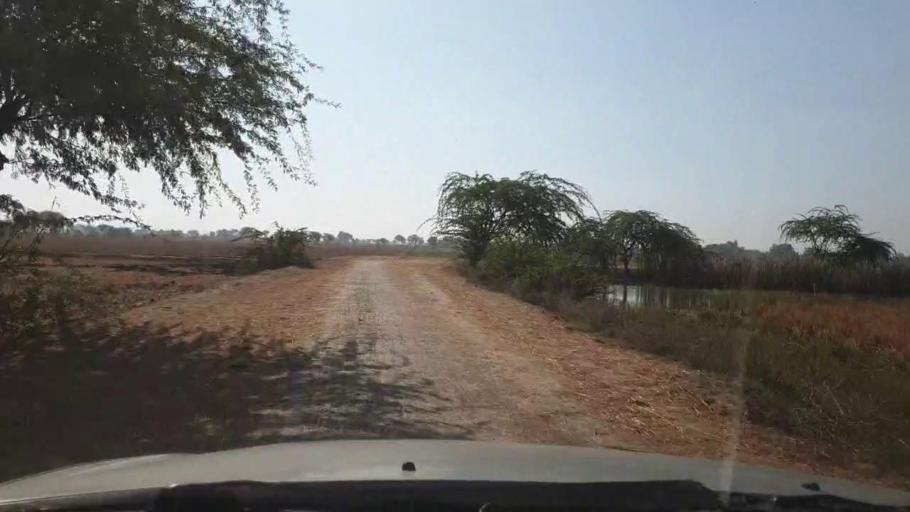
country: PK
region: Sindh
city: Kario
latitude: 24.8935
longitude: 68.5647
